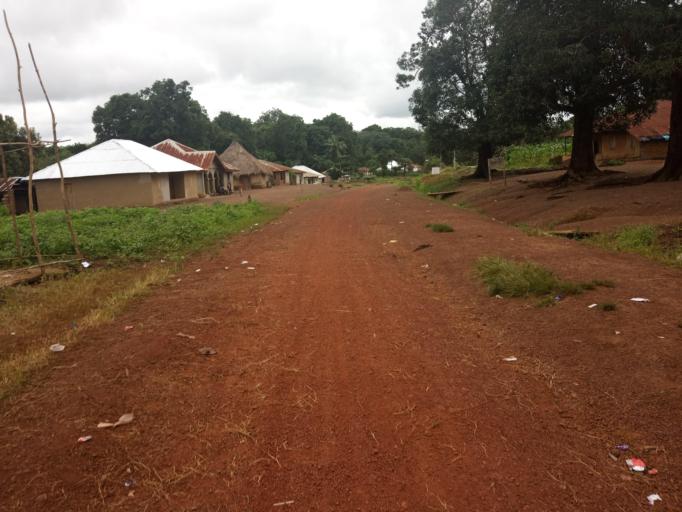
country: SL
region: Northern Province
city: Kamakwie
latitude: 9.5034
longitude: -12.2578
